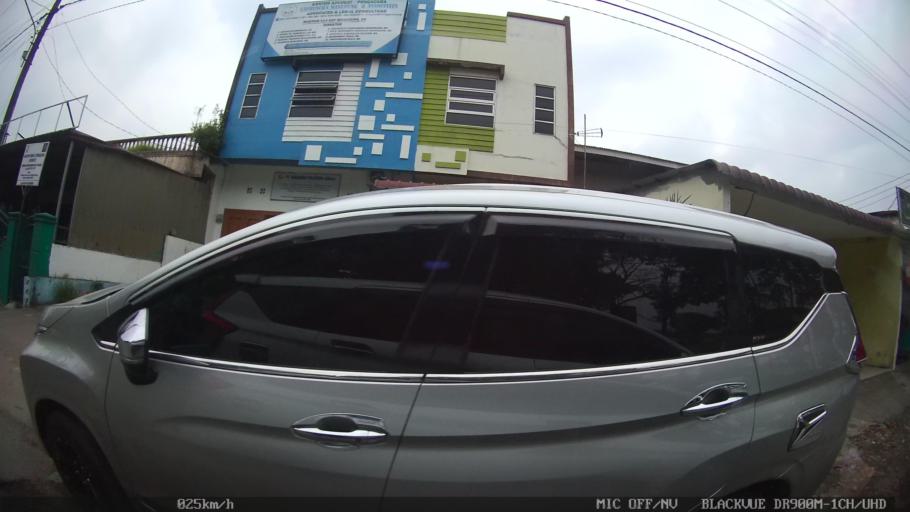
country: ID
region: North Sumatra
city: Deli Tua
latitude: 3.5414
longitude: 98.6985
